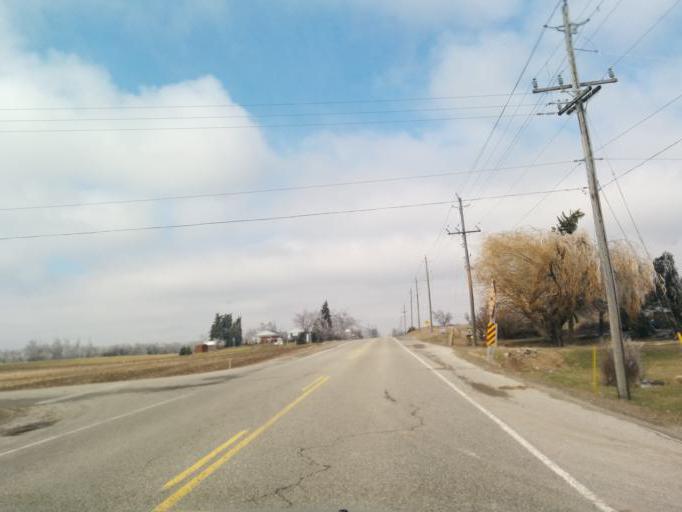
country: CA
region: Ontario
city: Waterloo
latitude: 43.6327
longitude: -80.5499
